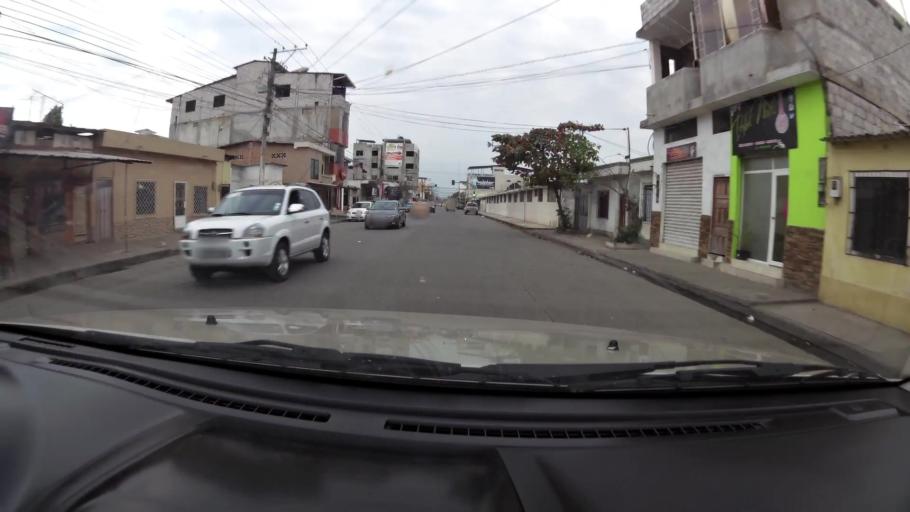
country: EC
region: El Oro
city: Machala
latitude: -3.2598
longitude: -79.9492
